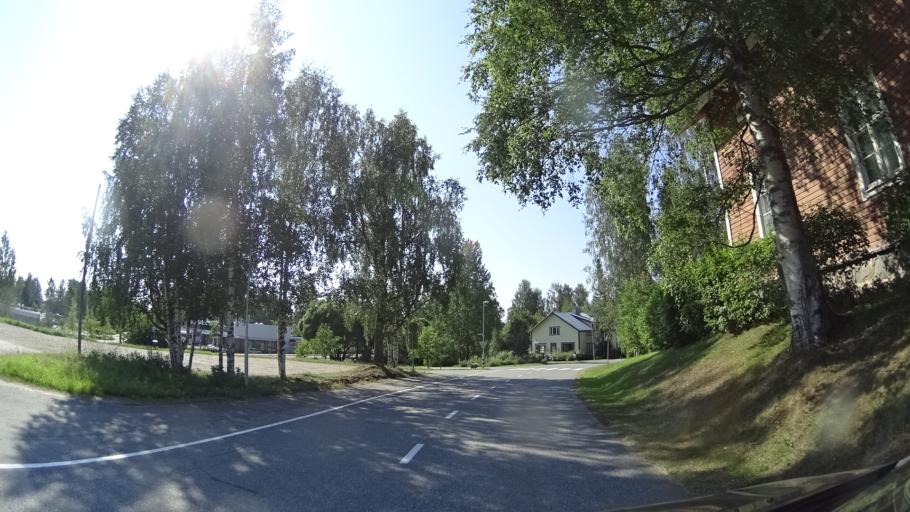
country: FI
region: North Karelia
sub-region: Joensuu
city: Juuka
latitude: 63.2410
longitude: 29.2504
